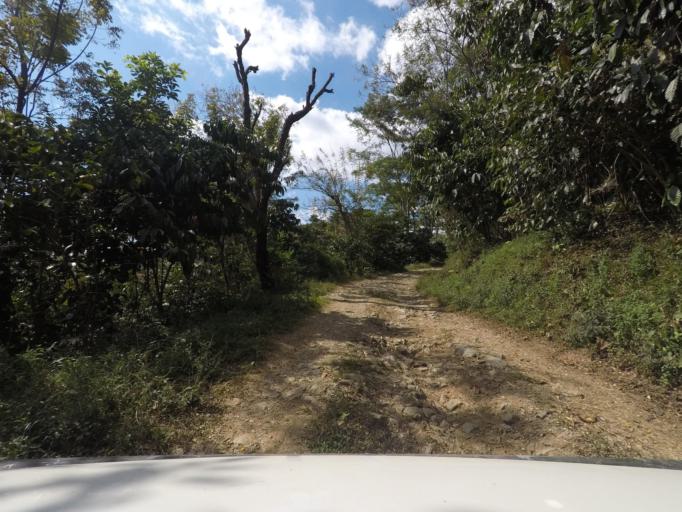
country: TL
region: Ermera
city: Gleno
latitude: -8.7189
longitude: 125.3094
